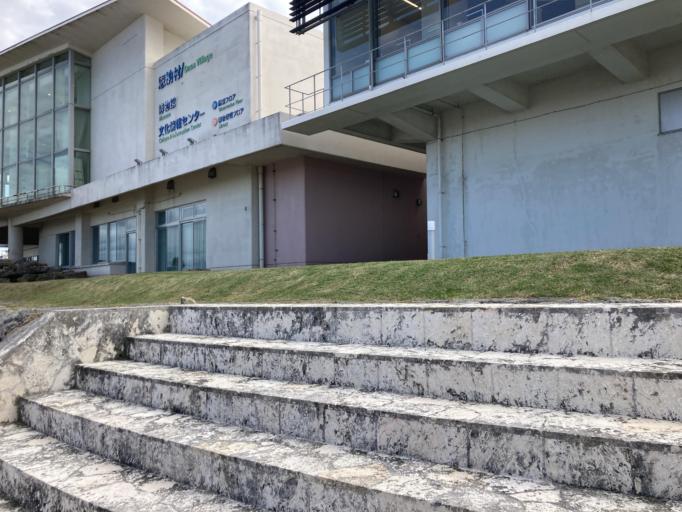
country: JP
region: Okinawa
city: Ishikawa
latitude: 26.4367
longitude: 127.7930
